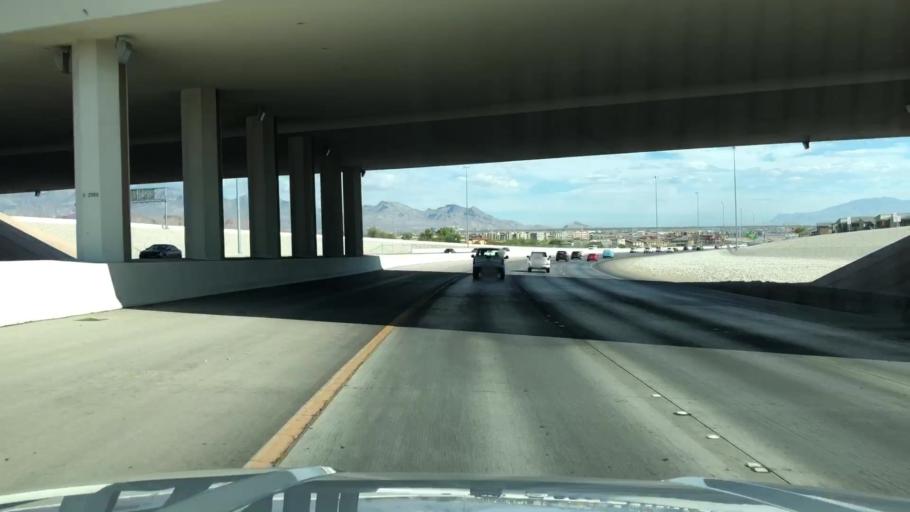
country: US
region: Nevada
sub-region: Clark County
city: Spring Valley
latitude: 36.0702
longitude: -115.2884
